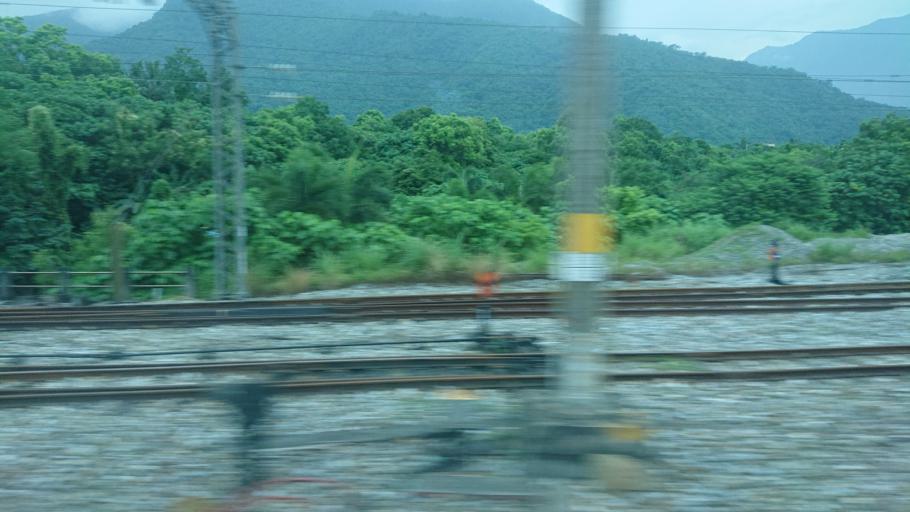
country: TW
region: Taiwan
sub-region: Hualien
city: Hualian
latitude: 24.1256
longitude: 121.6393
